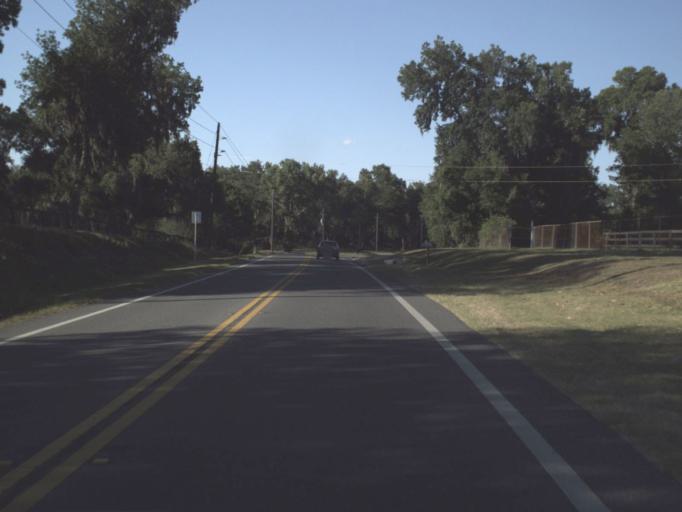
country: US
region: Florida
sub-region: Marion County
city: Dunnellon
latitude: 29.1655
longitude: -82.3405
